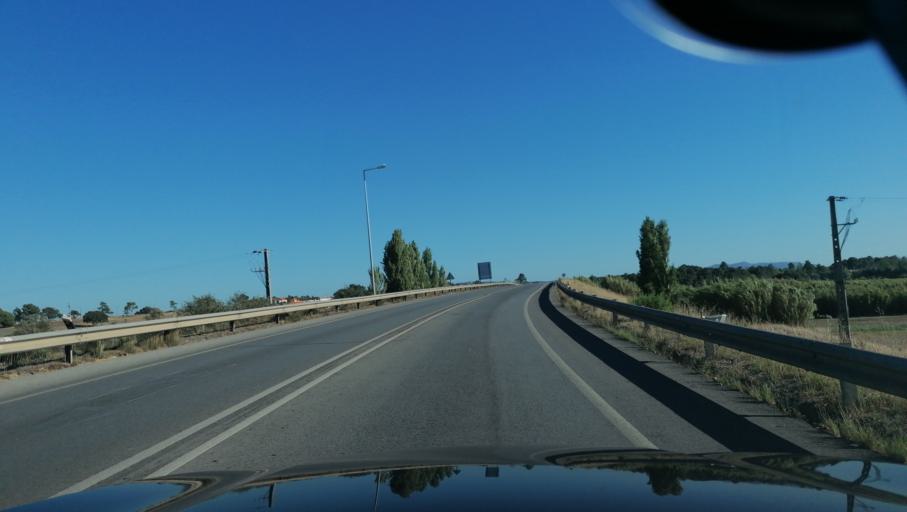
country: PT
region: Setubal
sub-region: Moita
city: Moita
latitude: 38.6420
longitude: -8.9719
